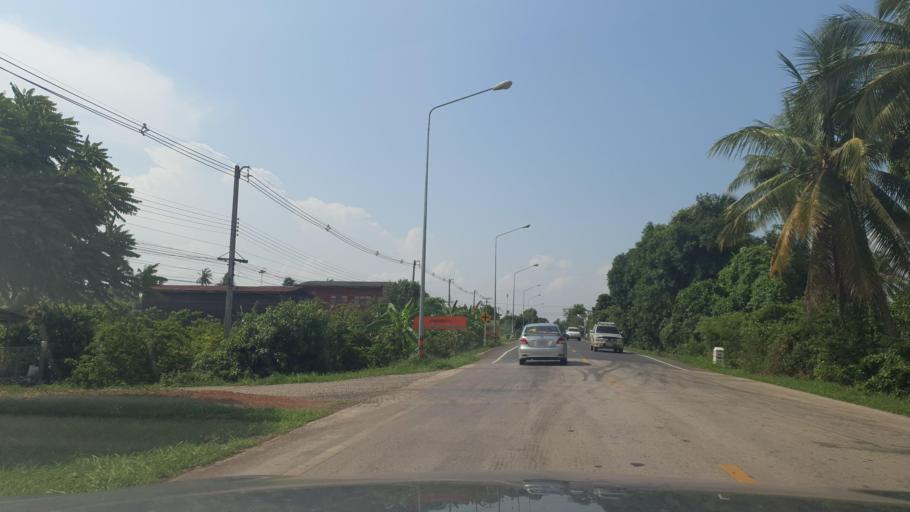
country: TH
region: Sukhothai
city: Si Samrong
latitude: 17.2023
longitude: 99.8488
